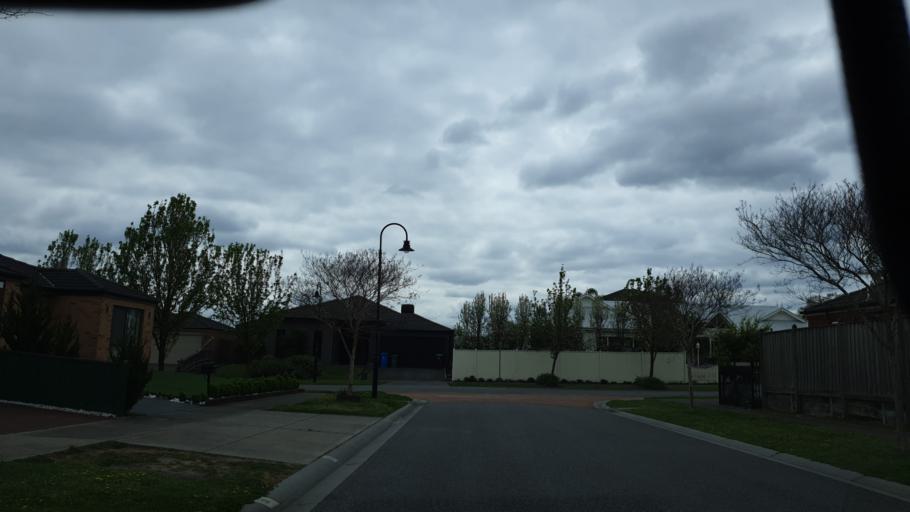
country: AU
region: Victoria
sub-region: Casey
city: Cranbourne North
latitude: -38.0736
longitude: 145.2896
